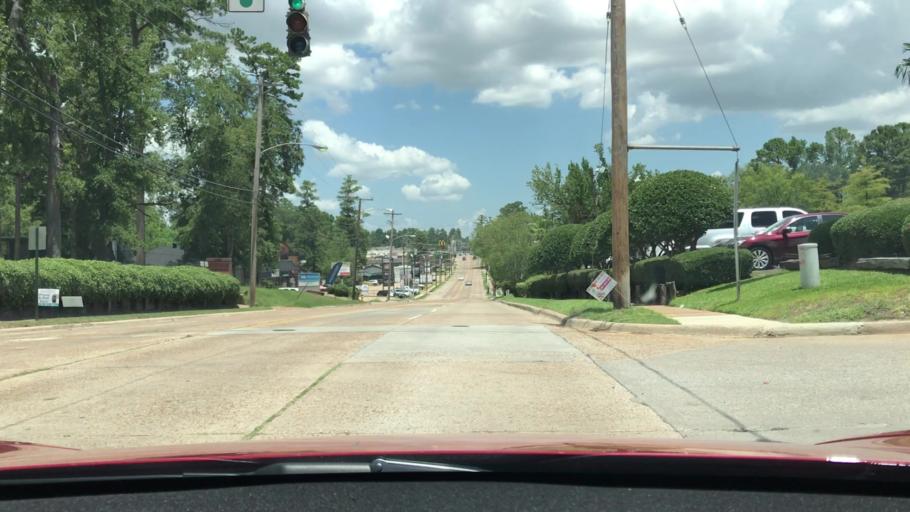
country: US
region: Louisiana
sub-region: Bossier Parish
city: Bossier City
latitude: 32.4493
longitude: -93.7460
